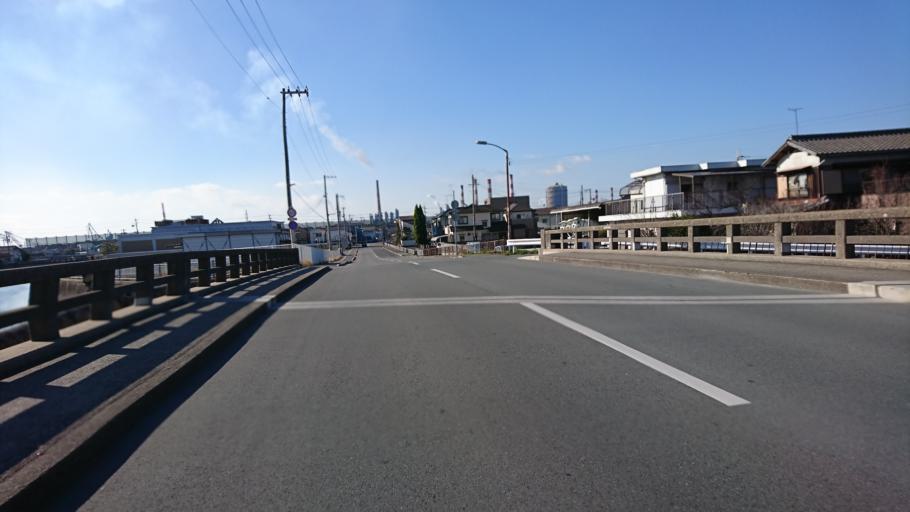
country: JP
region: Hyogo
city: Kakogawacho-honmachi
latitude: 34.7309
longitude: 134.8453
